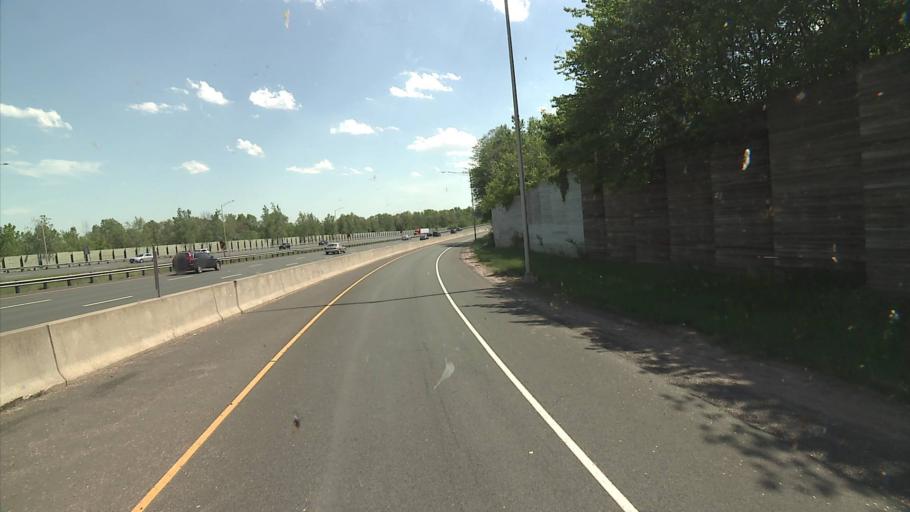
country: US
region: Connecticut
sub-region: New Haven County
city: Cheshire Village
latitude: 41.5852
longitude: -72.8993
